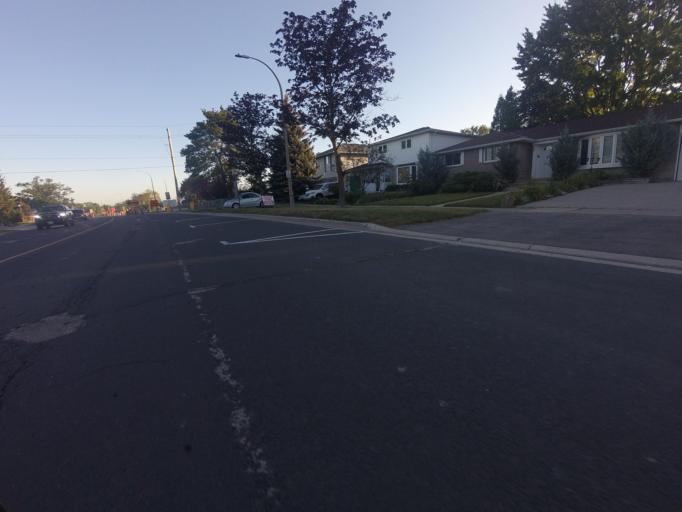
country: CA
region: Ontario
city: Bradford West Gwillimbury
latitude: 44.0281
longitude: -79.8071
